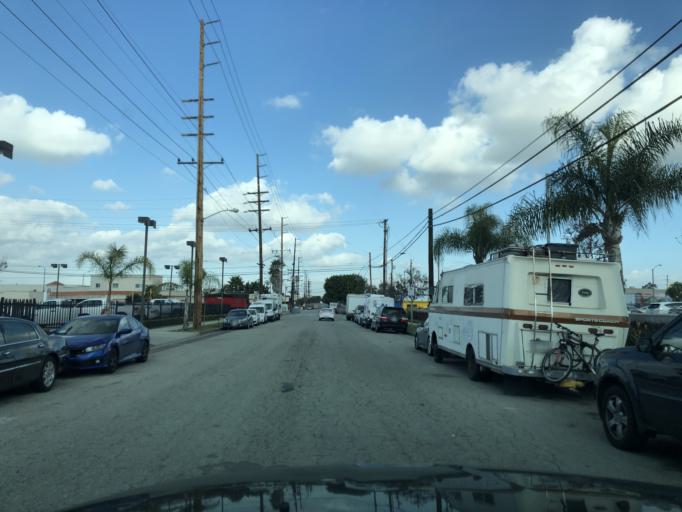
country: US
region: California
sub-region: Los Angeles County
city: Inglewood
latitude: 33.9591
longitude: -118.3718
